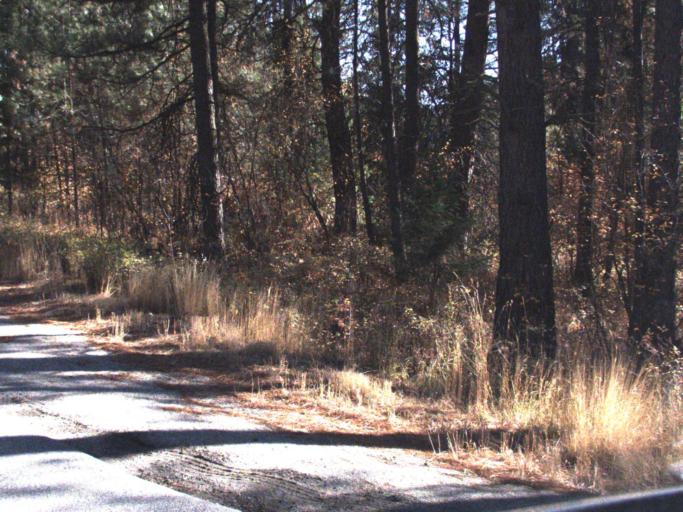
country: US
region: Washington
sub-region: Stevens County
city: Kettle Falls
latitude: 48.5922
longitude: -118.1682
